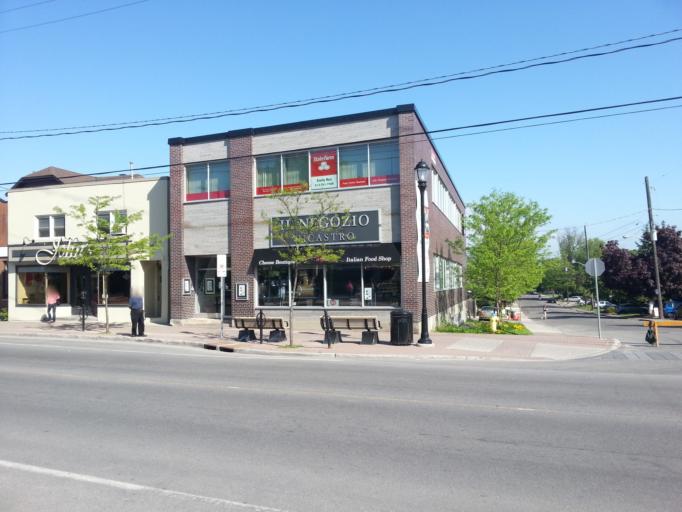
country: CA
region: Ontario
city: Ottawa
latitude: 45.3982
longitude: -75.7385
